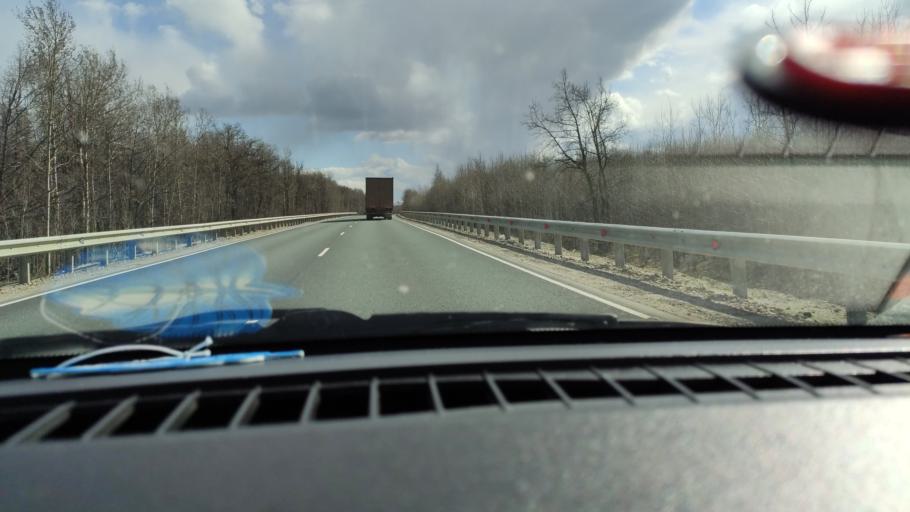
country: RU
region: Saratov
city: Khvalynsk
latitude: 52.4810
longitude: 48.0131
